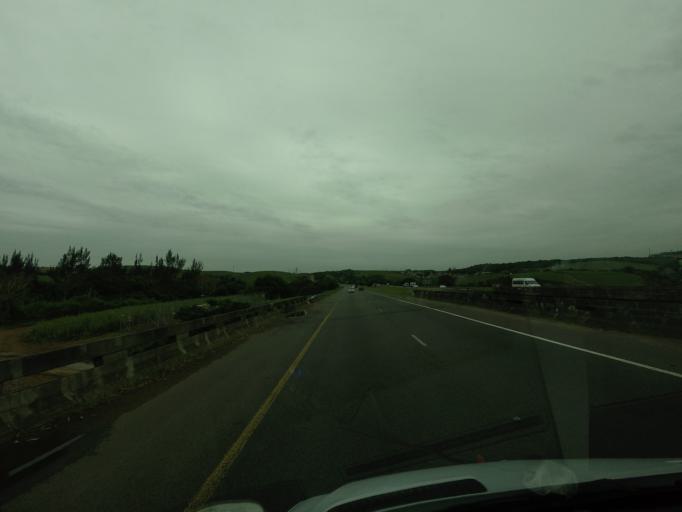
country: ZA
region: KwaZulu-Natal
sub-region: eThekwini Metropolitan Municipality
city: Durban
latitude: -29.6953
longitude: 31.0769
